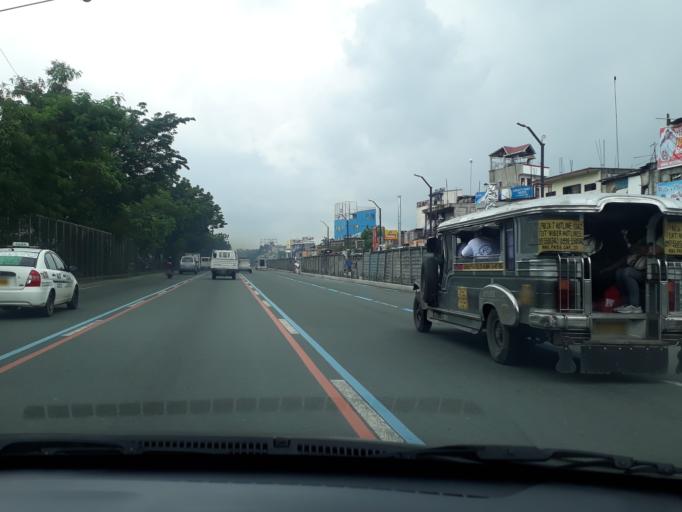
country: PH
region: Calabarzon
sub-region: Province of Rizal
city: Pateros
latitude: 14.5277
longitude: 121.0563
